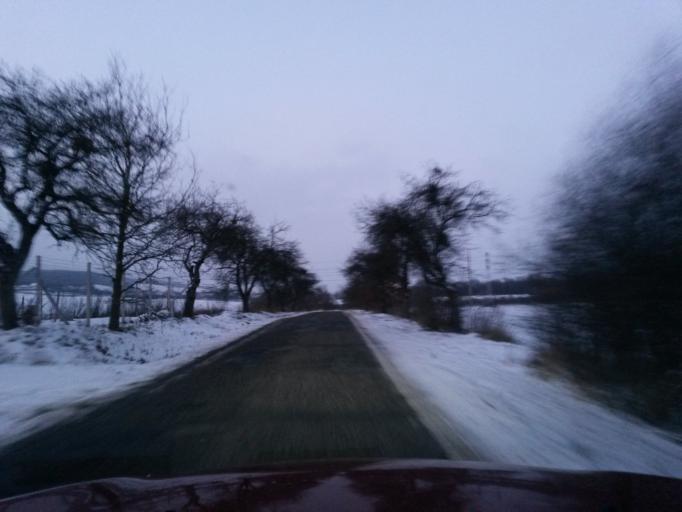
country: SK
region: Kosicky
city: Kosice
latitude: 48.7379
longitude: 21.3258
